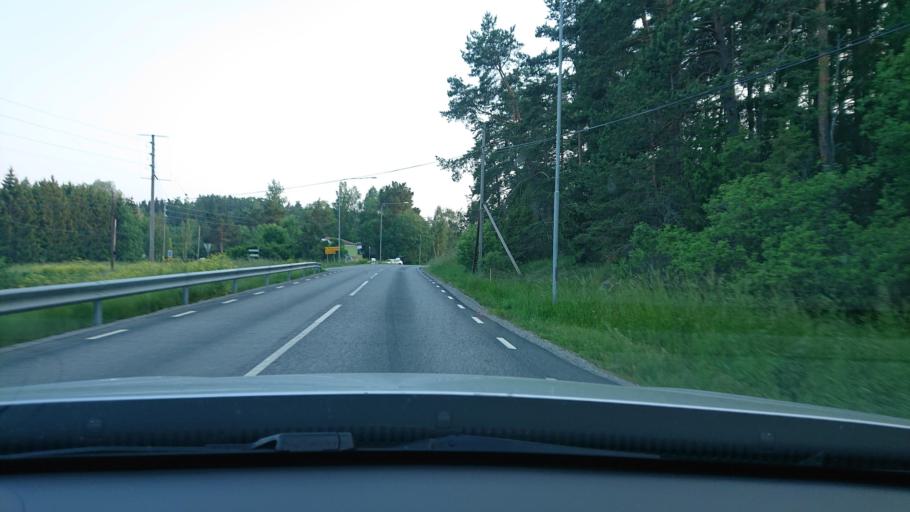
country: SE
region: Stockholm
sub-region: Vaxholms Kommun
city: Resaro
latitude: 59.4755
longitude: 18.3824
